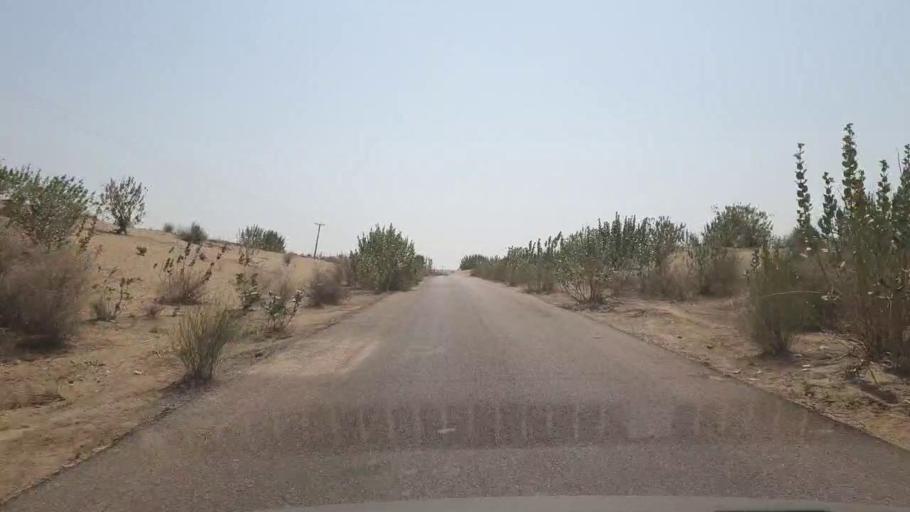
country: PK
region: Sindh
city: Chor
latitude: 25.6481
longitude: 70.1690
